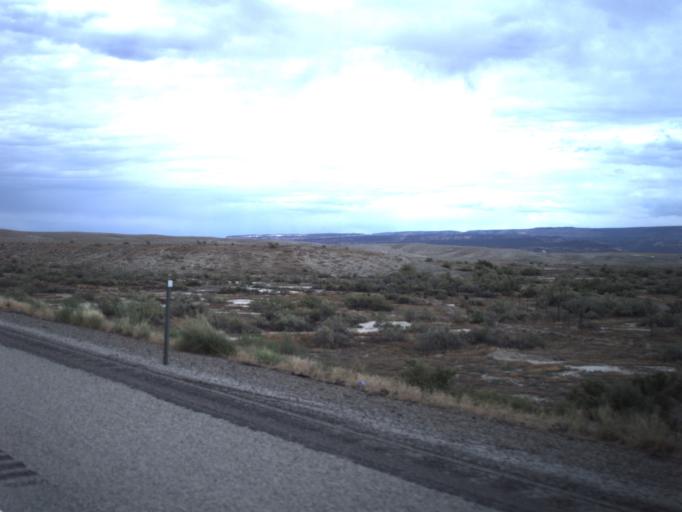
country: US
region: Utah
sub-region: Grand County
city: Moab
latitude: 38.9763
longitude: -109.3500
